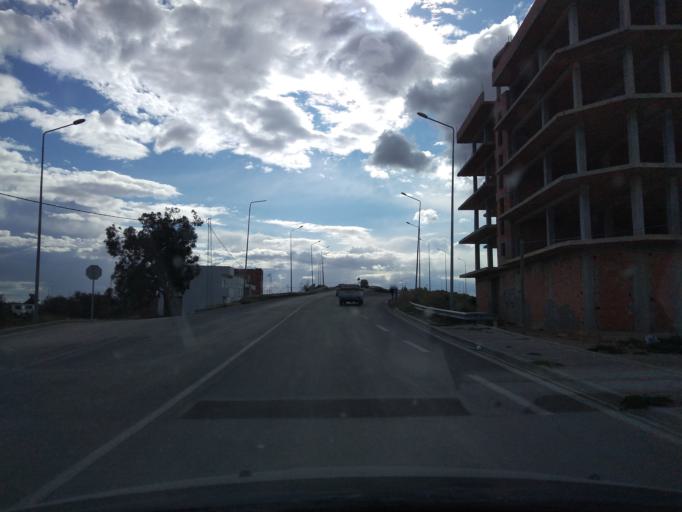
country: TN
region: Susah
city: Masakin
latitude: 35.7133
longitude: 10.5605
